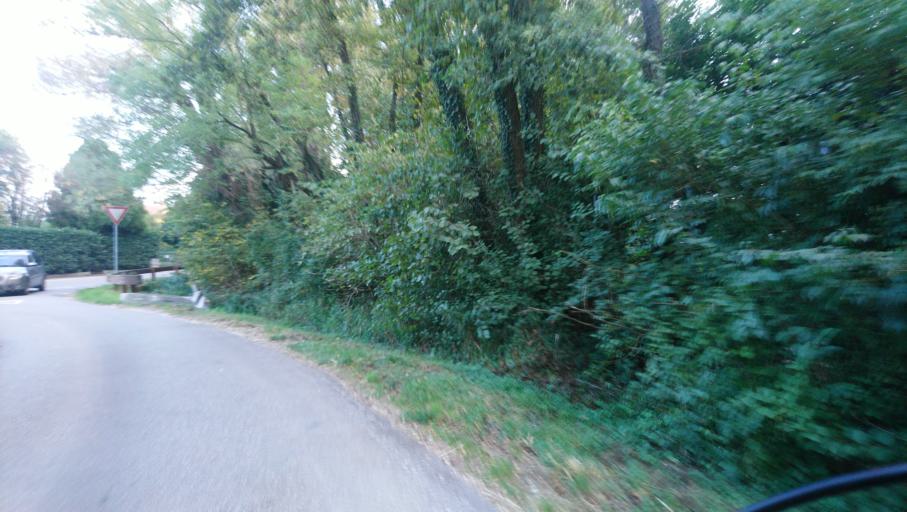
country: IT
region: Veneto
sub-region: Provincia di Treviso
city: Treviso
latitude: 45.6889
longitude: 12.2420
